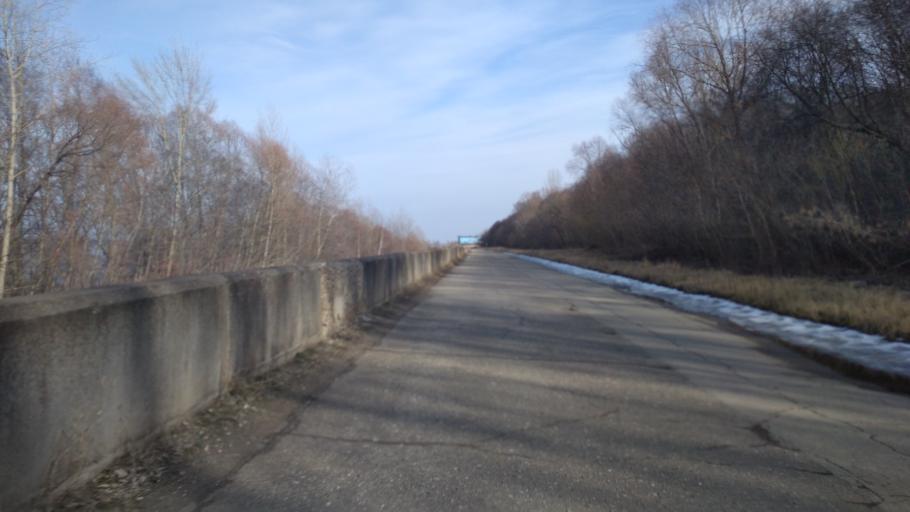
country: RU
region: Chuvashia
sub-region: Cheboksarskiy Rayon
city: Cheboksary
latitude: 56.1457
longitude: 47.3150
